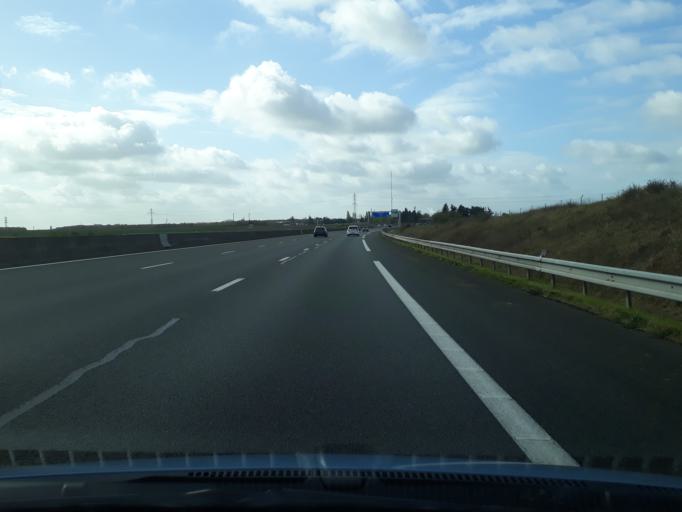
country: FR
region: Centre
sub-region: Departement du Loir-et-Cher
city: La Chaussee-Saint-Victor
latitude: 47.6303
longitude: 1.3531
